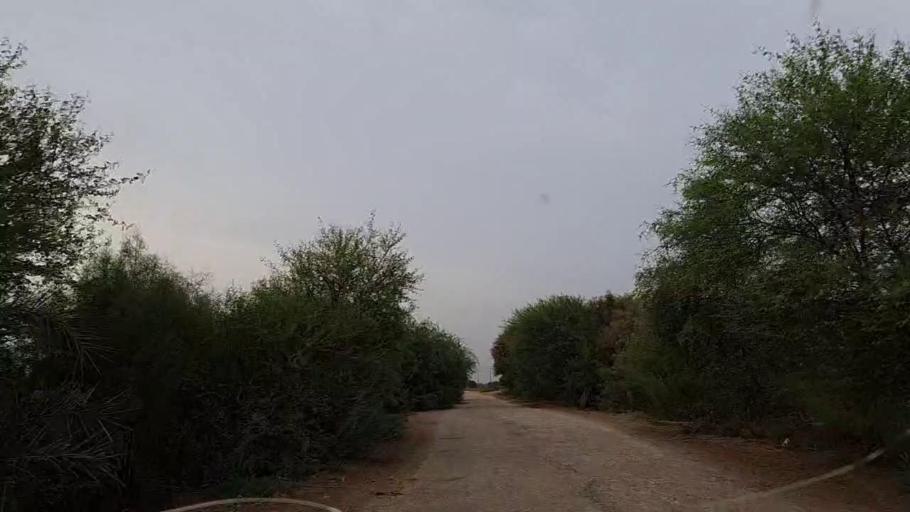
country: PK
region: Sindh
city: Mirpur Mathelo
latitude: 27.8514
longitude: 69.6302
